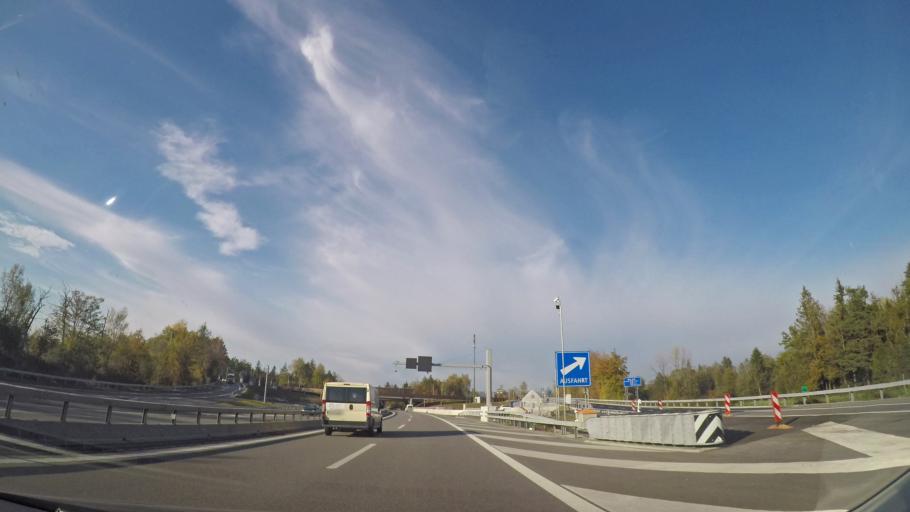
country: CH
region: Bern
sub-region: Bern-Mittelland District
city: Rubigen
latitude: 46.8882
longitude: 7.5406
